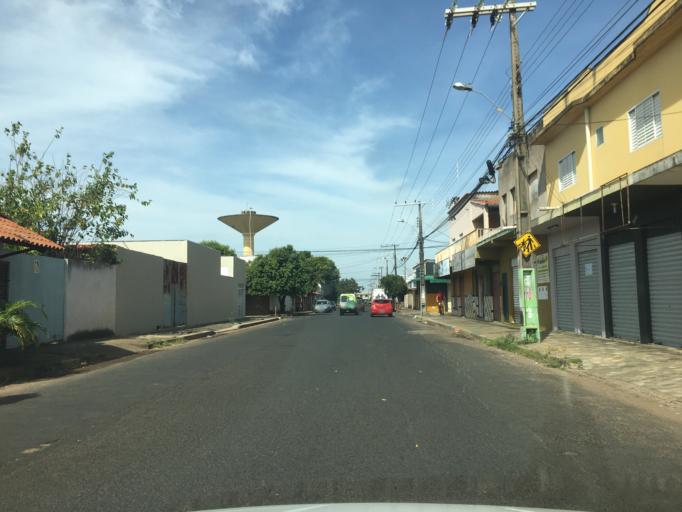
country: BR
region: Minas Gerais
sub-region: Uberlandia
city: Uberlandia
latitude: -18.9427
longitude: -48.3122
